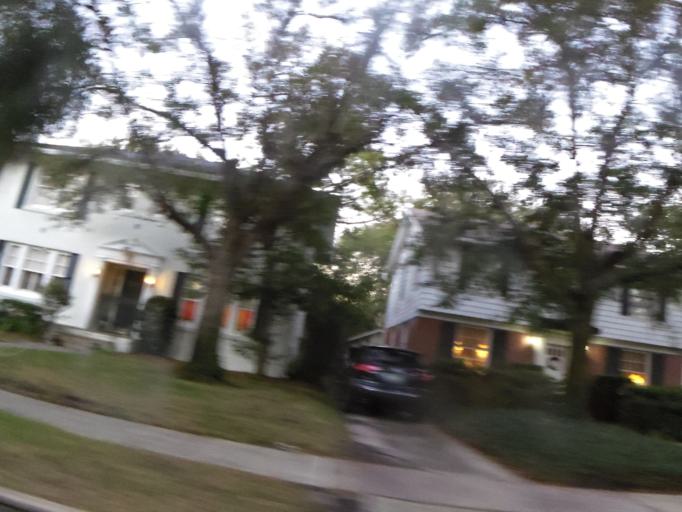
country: US
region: Florida
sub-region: Duval County
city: Jacksonville
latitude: 30.2964
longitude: -81.7009
